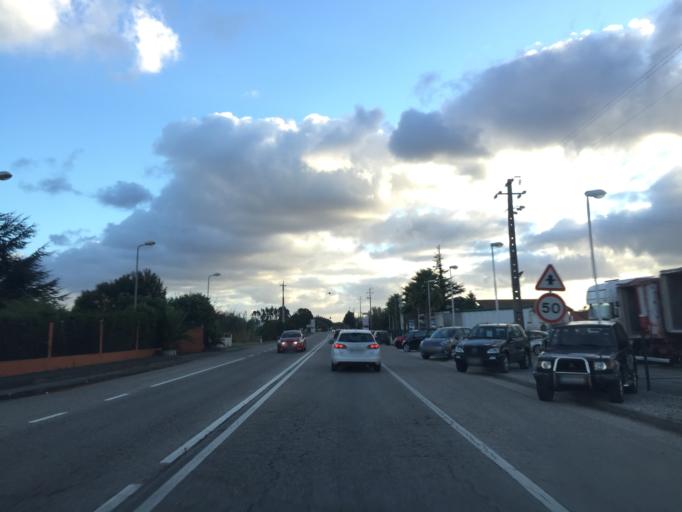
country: PT
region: Leiria
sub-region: Alcobaca
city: Benedita
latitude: 39.4296
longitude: -8.9586
